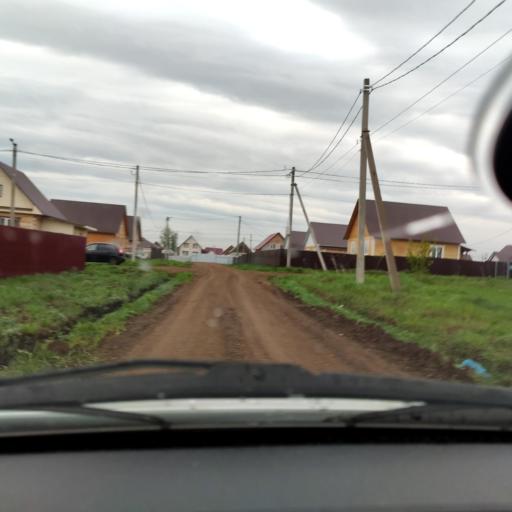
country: RU
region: Bashkortostan
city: Iglino
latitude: 54.8266
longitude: 56.4271
